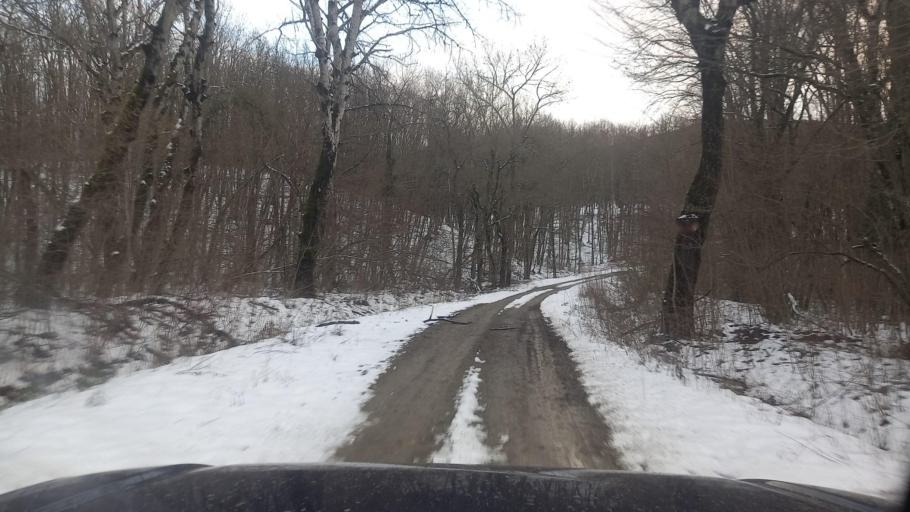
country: RU
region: Krasnodarskiy
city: Smolenskaya
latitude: 44.6789
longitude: 38.7837
